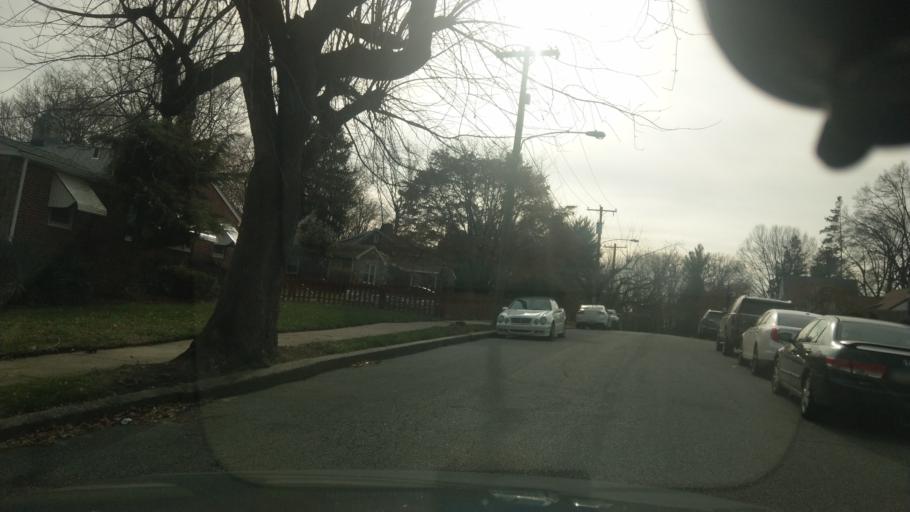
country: US
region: Pennsylvania
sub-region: Montgomery County
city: Wyncote
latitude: 40.0493
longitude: -75.1364
